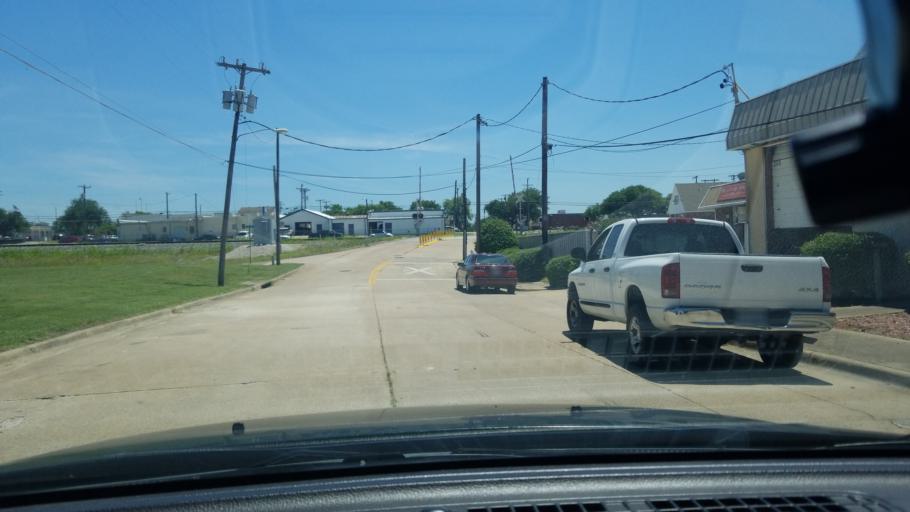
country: US
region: Texas
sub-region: Dallas County
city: Mesquite
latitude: 32.7686
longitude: -96.6019
